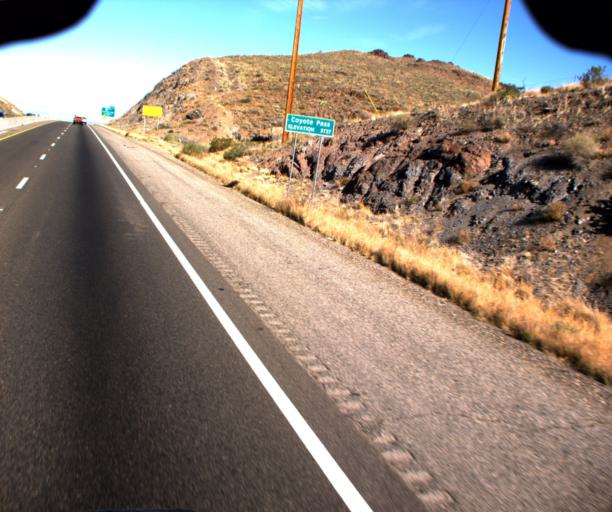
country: US
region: Arizona
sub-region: Mohave County
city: Kingman
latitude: 35.2080
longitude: -114.1002
